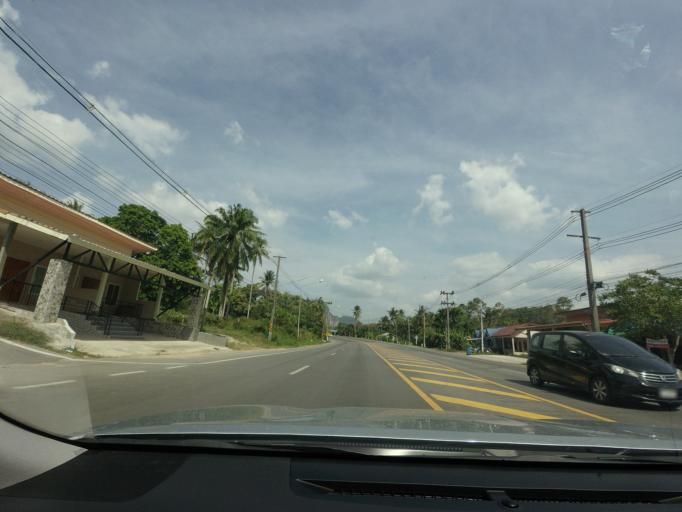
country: TH
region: Phangnga
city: Ban Ao Nang
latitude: 8.0571
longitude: 98.7799
